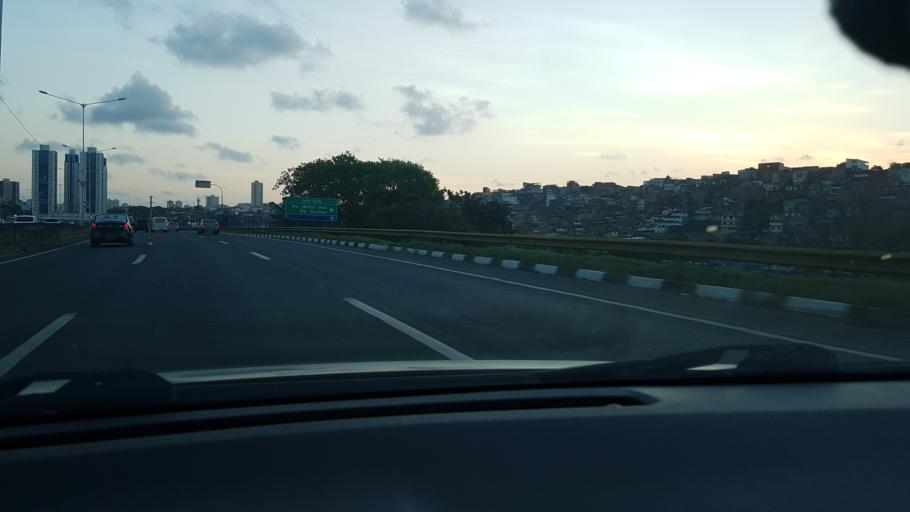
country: BR
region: Bahia
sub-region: Salvador
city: Salvador
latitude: -12.9616
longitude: -38.4755
